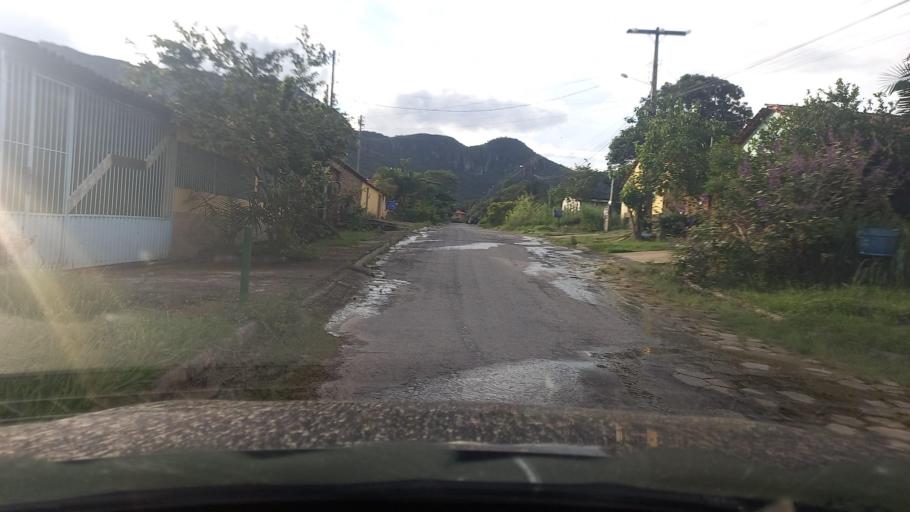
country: BR
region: Goias
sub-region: Cavalcante
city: Cavalcante
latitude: -13.7939
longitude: -47.4614
